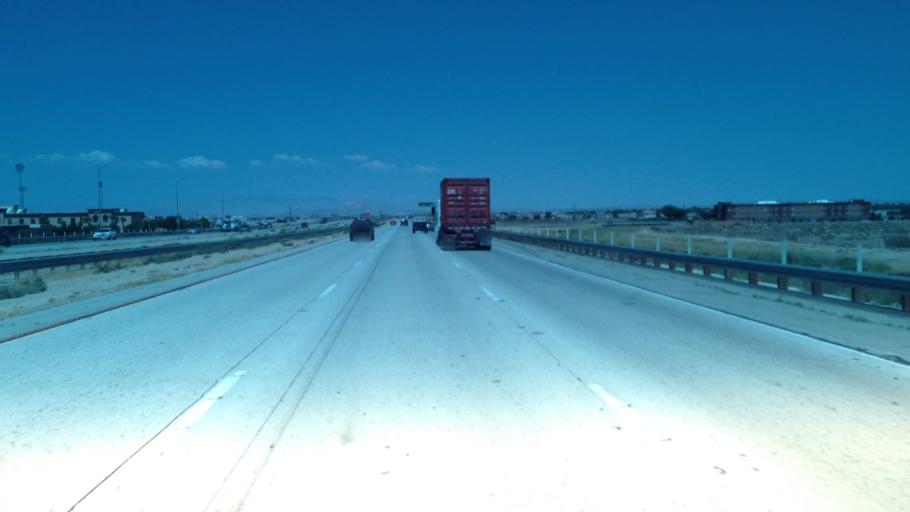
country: US
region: California
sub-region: Los Angeles County
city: Lancaster
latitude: 34.6981
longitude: -118.1689
